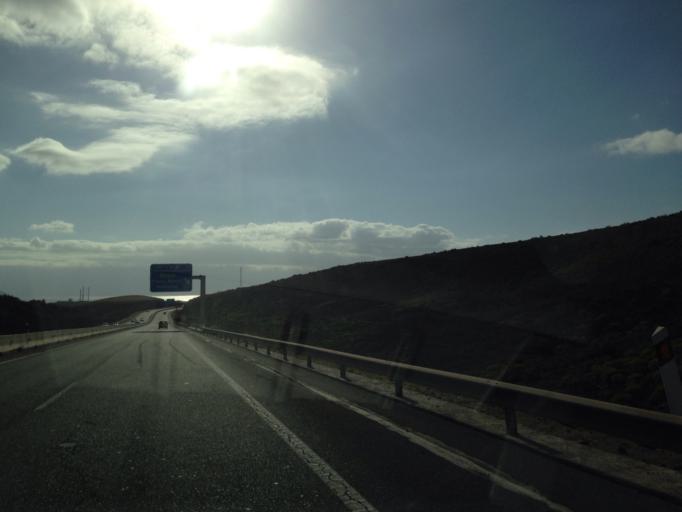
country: ES
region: Canary Islands
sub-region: Provincia de Las Palmas
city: Maspalomas
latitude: 27.7655
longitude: -15.6296
